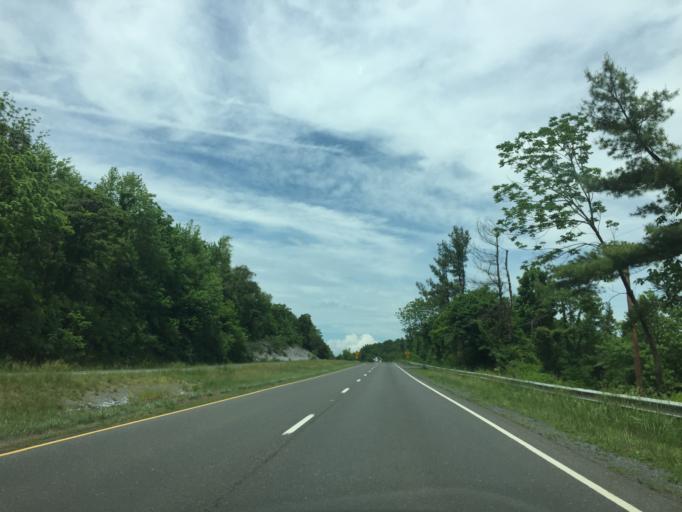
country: US
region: Virginia
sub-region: City of Winchester
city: Winchester
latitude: 39.2346
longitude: -78.1999
